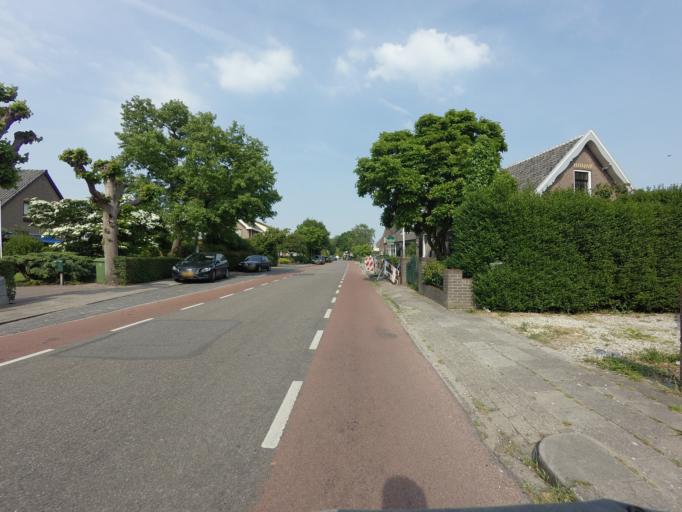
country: NL
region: North Holland
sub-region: Gemeente Wijdemeren
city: Nieuw-Loosdrecht
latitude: 52.1939
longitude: 5.1244
